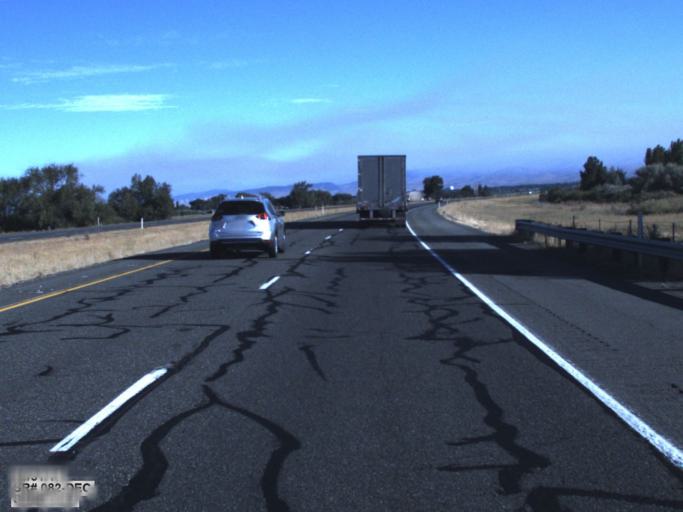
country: US
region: Washington
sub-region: Kittitas County
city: Ellensburg
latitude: 46.9360
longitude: -120.5059
